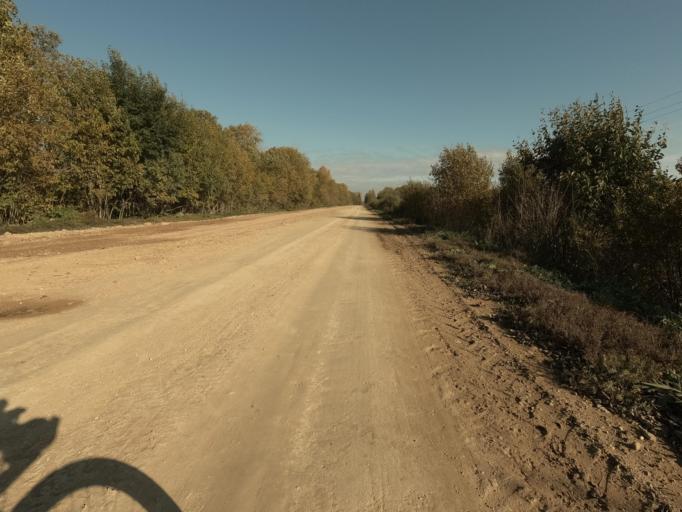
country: RU
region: Novgorod
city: Batetskiy
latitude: 58.8233
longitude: 30.7062
